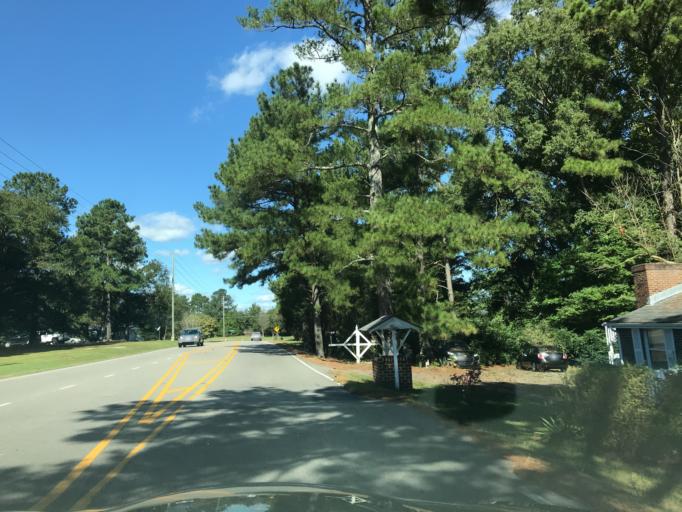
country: US
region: North Carolina
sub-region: Wake County
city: Wake Forest
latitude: 35.9325
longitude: -78.5053
